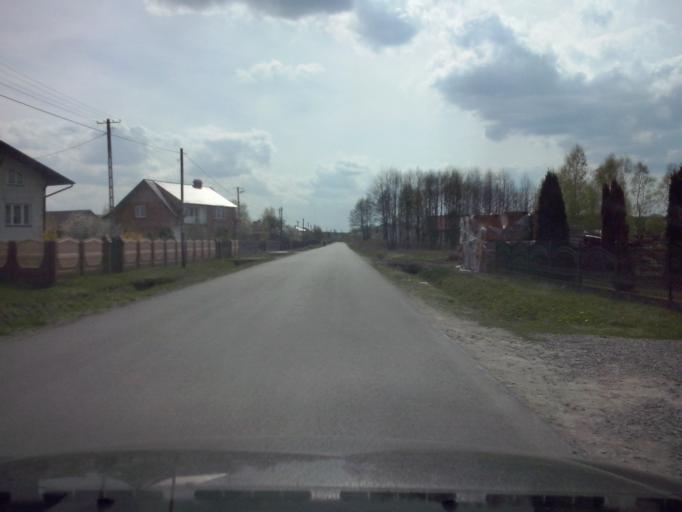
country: PL
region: Subcarpathian Voivodeship
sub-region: Powiat lezajski
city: Letownia
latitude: 50.3522
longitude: 22.2033
